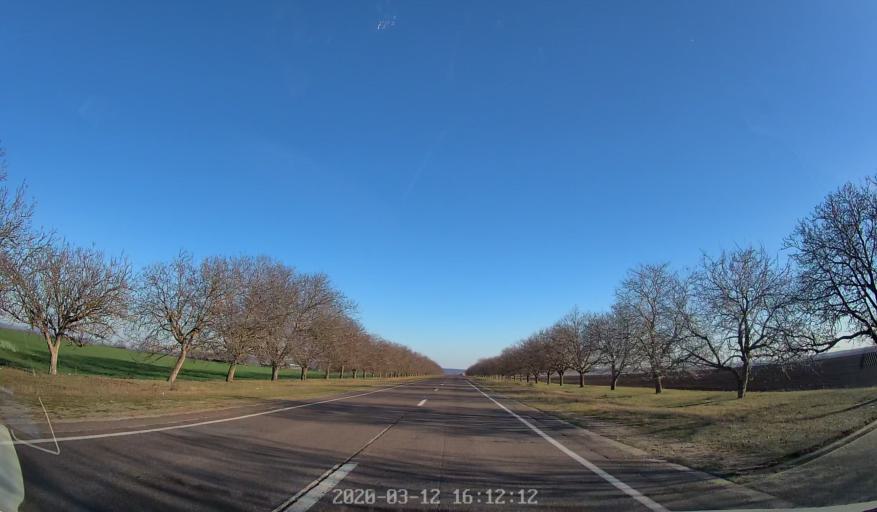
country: MD
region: Anenii Noi
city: Anenii Noi
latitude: 46.9385
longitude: 29.2694
